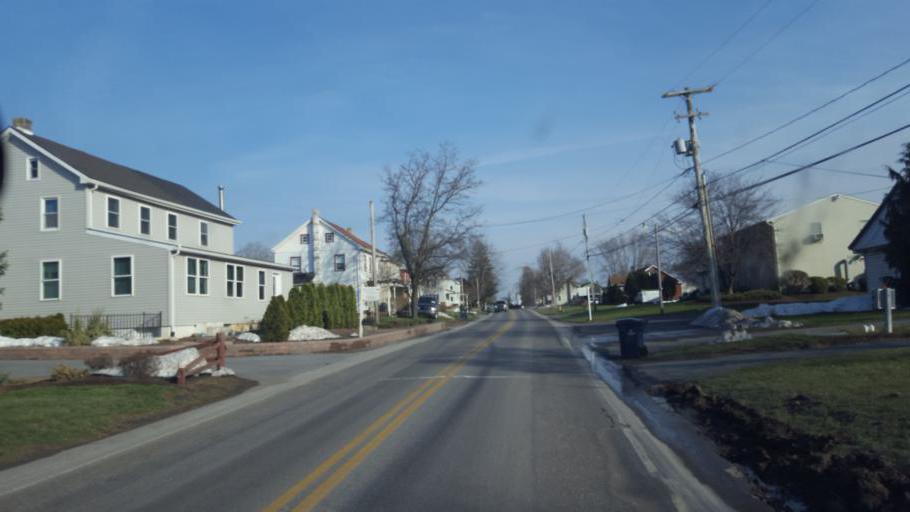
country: US
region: Pennsylvania
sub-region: Lancaster County
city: Brownstown
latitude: 40.0725
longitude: -76.1750
